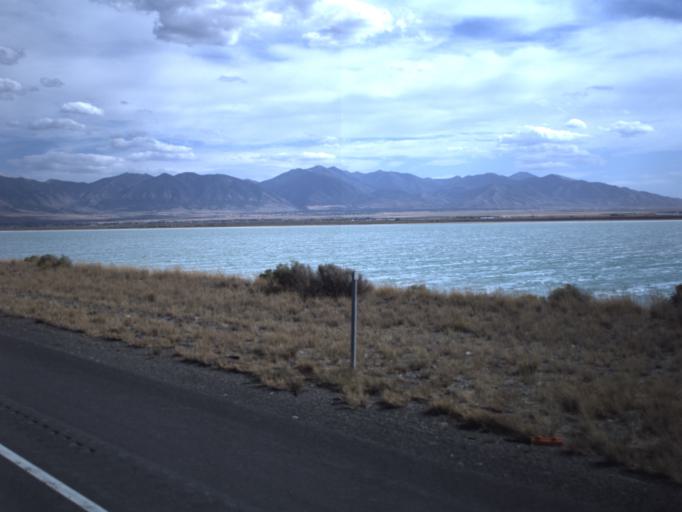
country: US
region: Utah
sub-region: Tooele County
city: Grantsville
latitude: 40.6738
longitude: -112.3972
